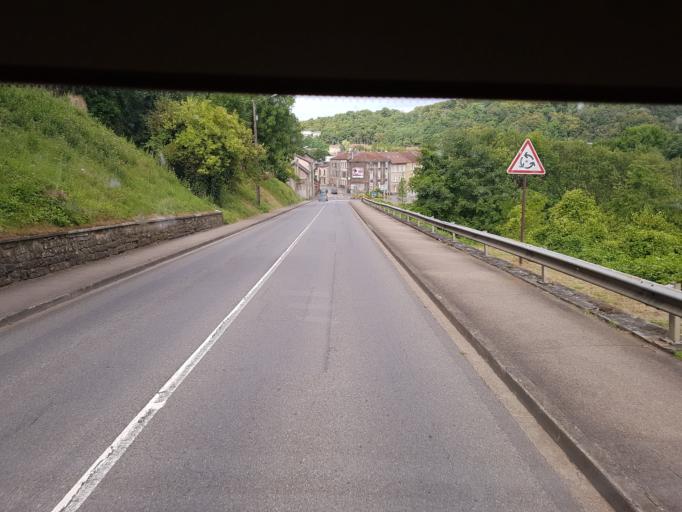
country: FR
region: Lorraine
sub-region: Departement de Meurthe-et-Moselle
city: Homecourt
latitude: 49.2249
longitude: 5.9978
